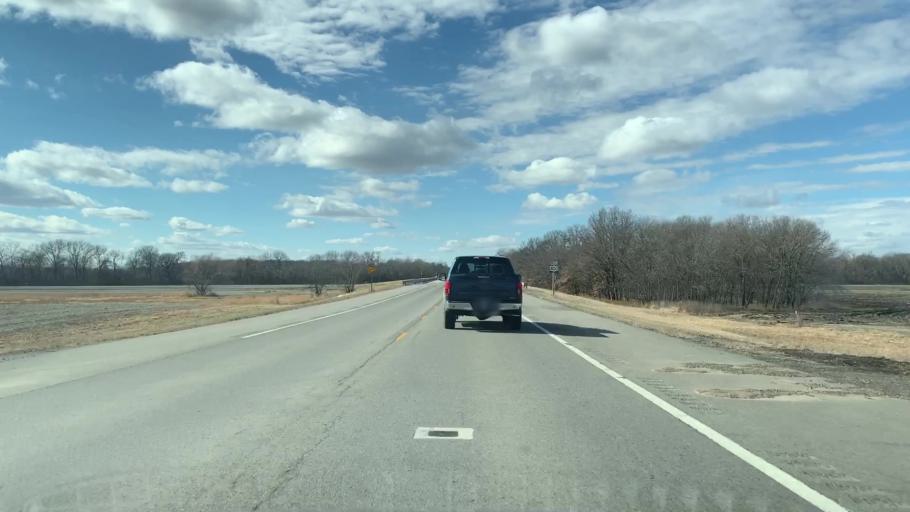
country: US
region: Kansas
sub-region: Cherokee County
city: Columbus
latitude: 37.3401
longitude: -94.9589
